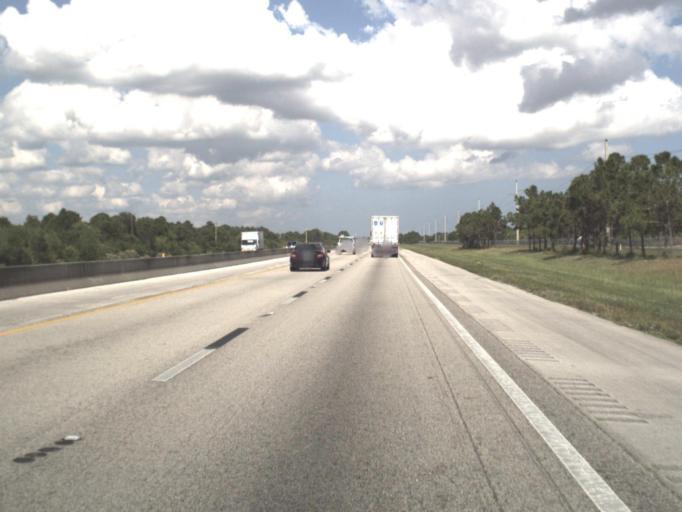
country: US
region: Florida
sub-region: Saint Lucie County
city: River Park
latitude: 27.3218
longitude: -80.3742
